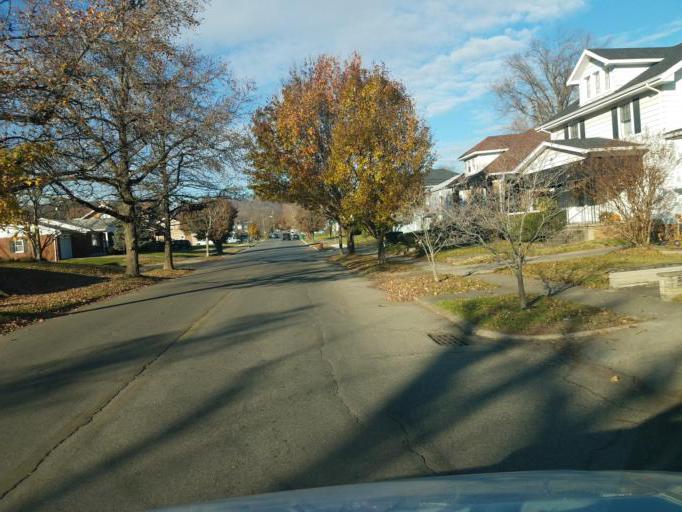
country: US
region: Ohio
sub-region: Scioto County
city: Portsmouth
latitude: 38.7494
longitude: -82.9749
